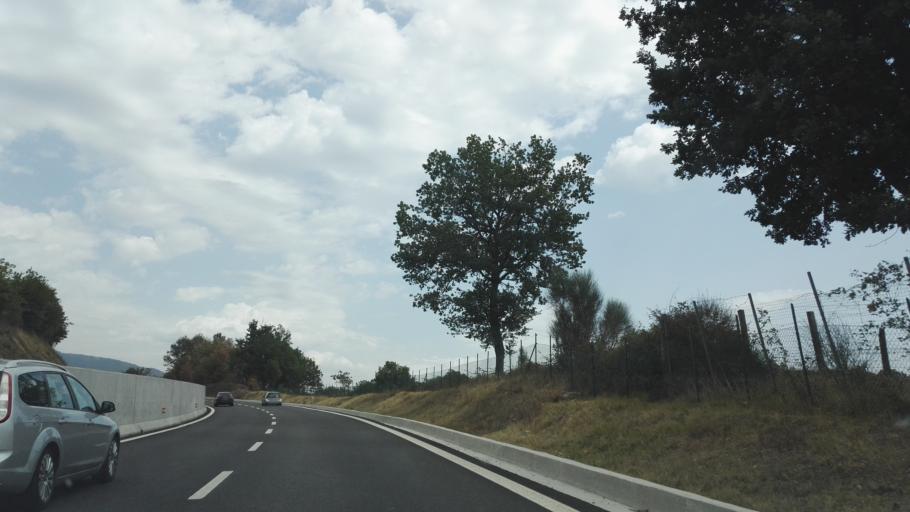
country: IT
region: Calabria
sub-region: Provincia di Cosenza
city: Laino Borgo
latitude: 39.9715
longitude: 15.9350
